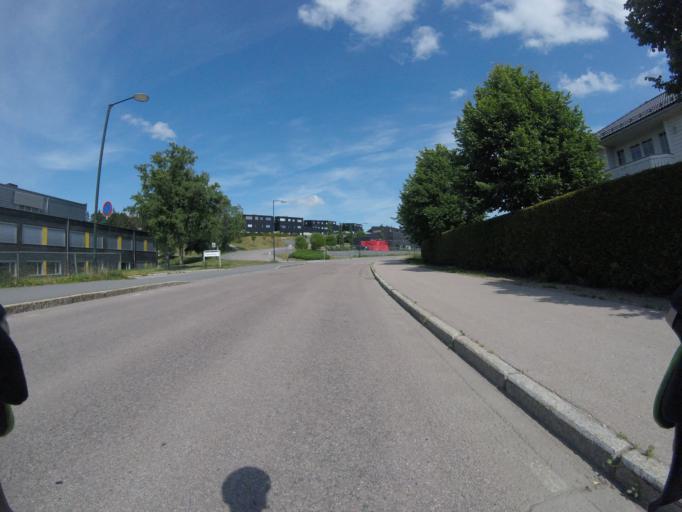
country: NO
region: Akershus
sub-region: Skedsmo
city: Lillestrom
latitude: 59.9743
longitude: 11.0410
